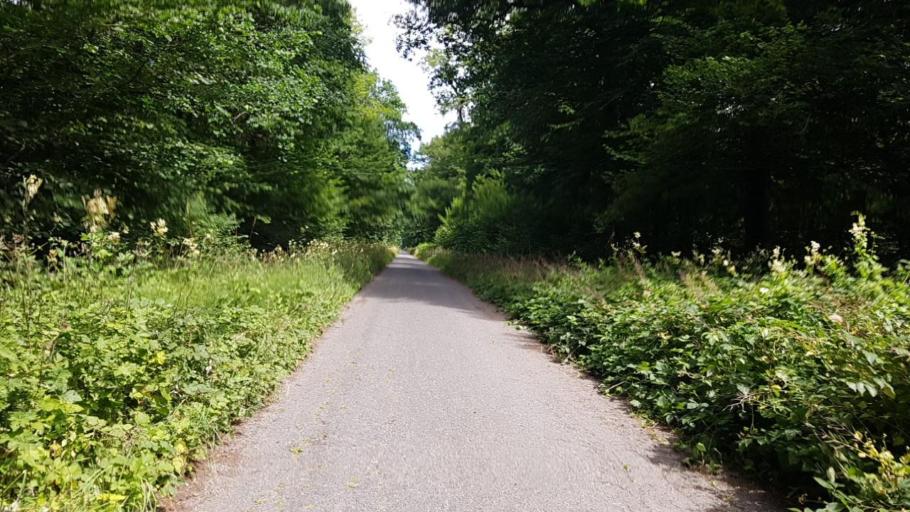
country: FR
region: Picardie
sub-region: Departement de l'Oise
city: Montmacq
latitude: 49.4660
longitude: 2.9088
